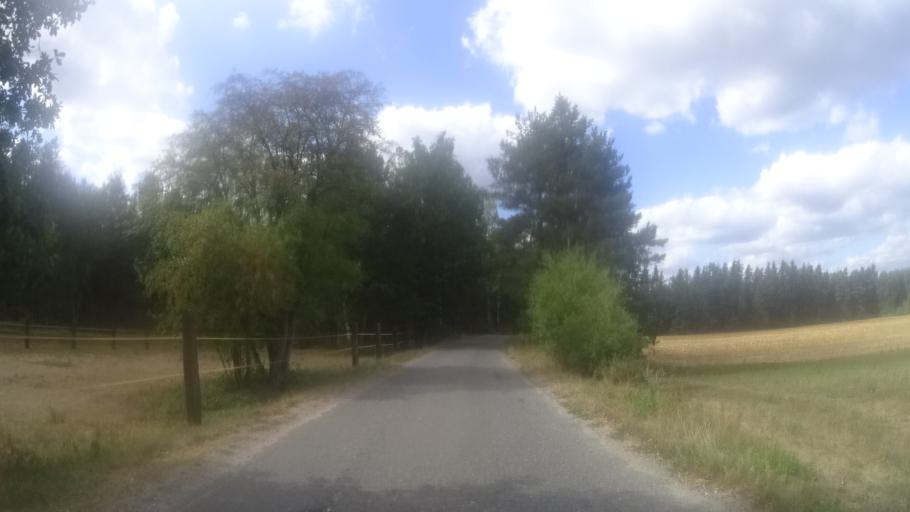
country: CZ
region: Pardubicky
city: Horni Jeleni
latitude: 50.0593
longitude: 16.1462
